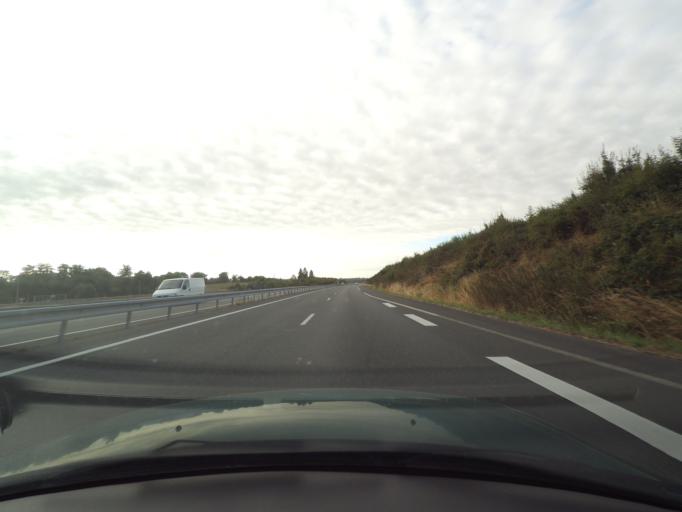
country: FR
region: Pays de la Loire
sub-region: Departement de Maine-et-Loire
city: La Tessoualle
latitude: 46.9700
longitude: -0.8034
